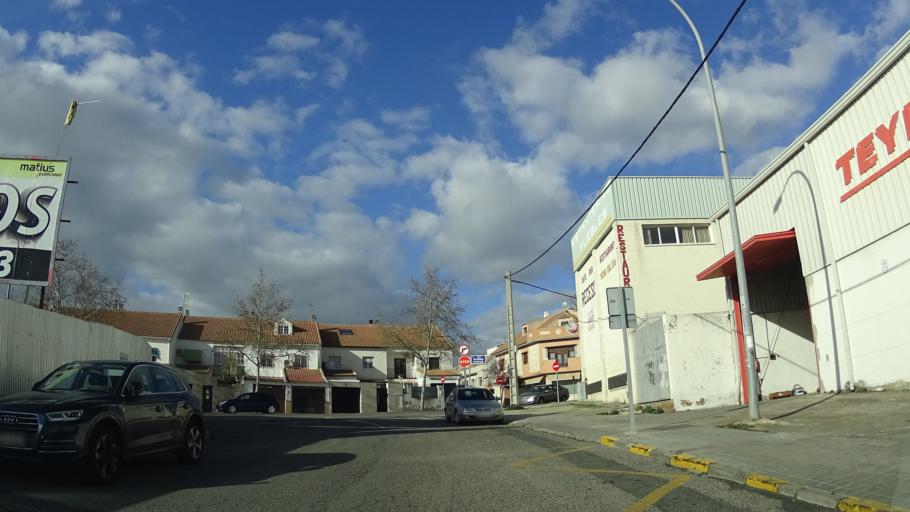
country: ES
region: Castille-La Mancha
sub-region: Provincia de Ciudad Real
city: Ciudad Real
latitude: 38.9775
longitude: -3.9307
